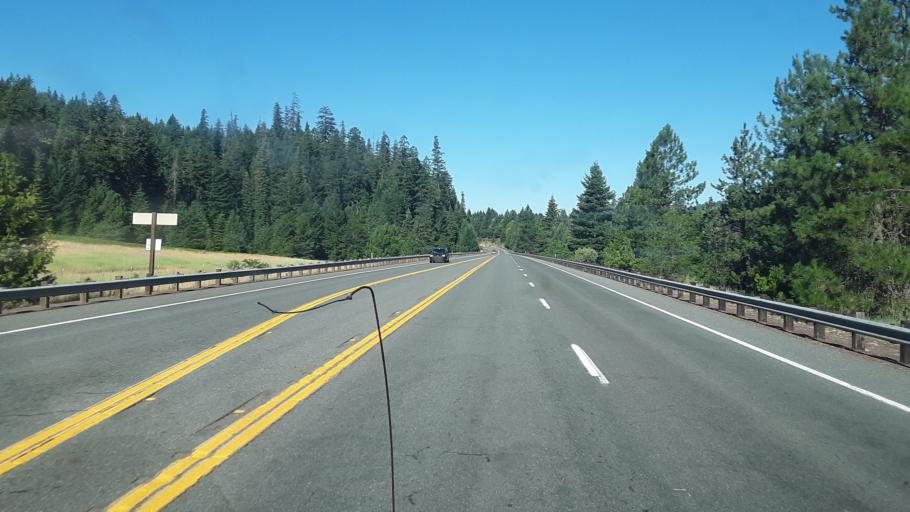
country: US
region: Oregon
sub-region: Jackson County
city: Shady Cove
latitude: 42.6743
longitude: -122.6265
